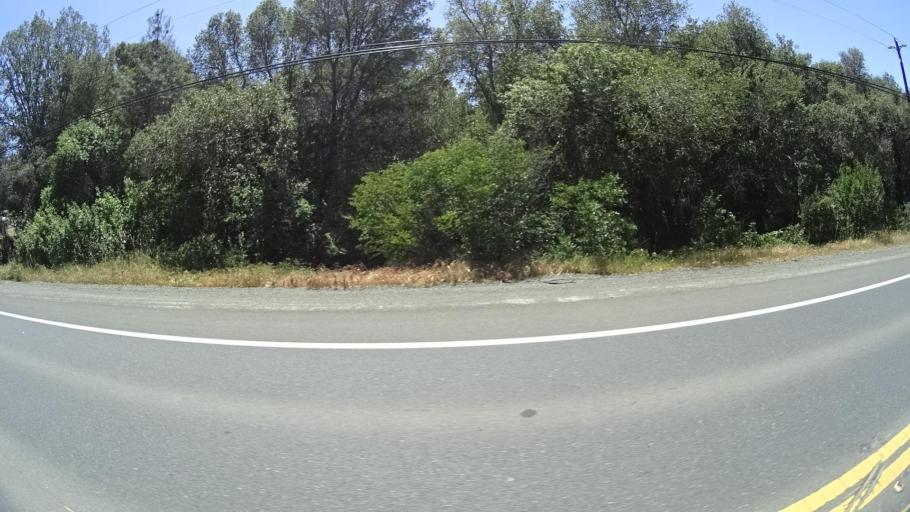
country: US
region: California
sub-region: Lake County
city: Clearlake Oaks
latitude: 39.0178
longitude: -122.6441
